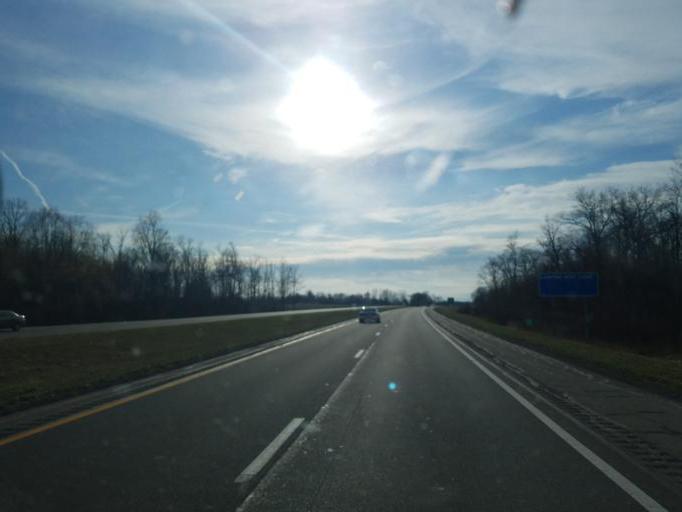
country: US
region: Ohio
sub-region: Crawford County
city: Galion
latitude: 40.7612
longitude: -82.7649
